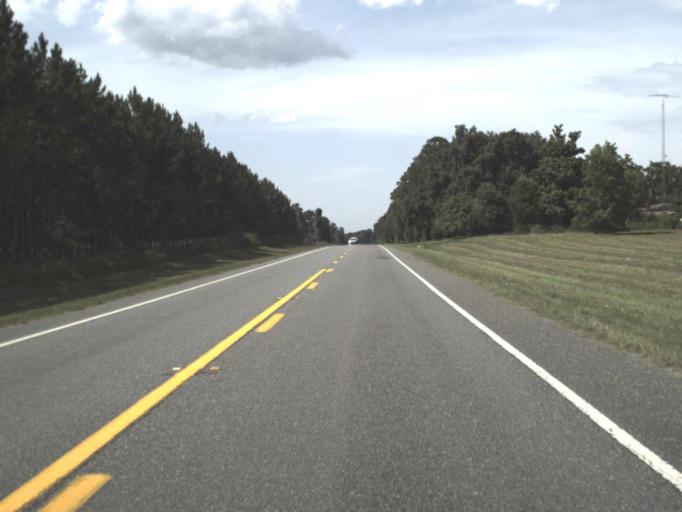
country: US
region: Florida
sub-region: Columbia County
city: Lake City
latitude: 30.0192
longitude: -82.7102
